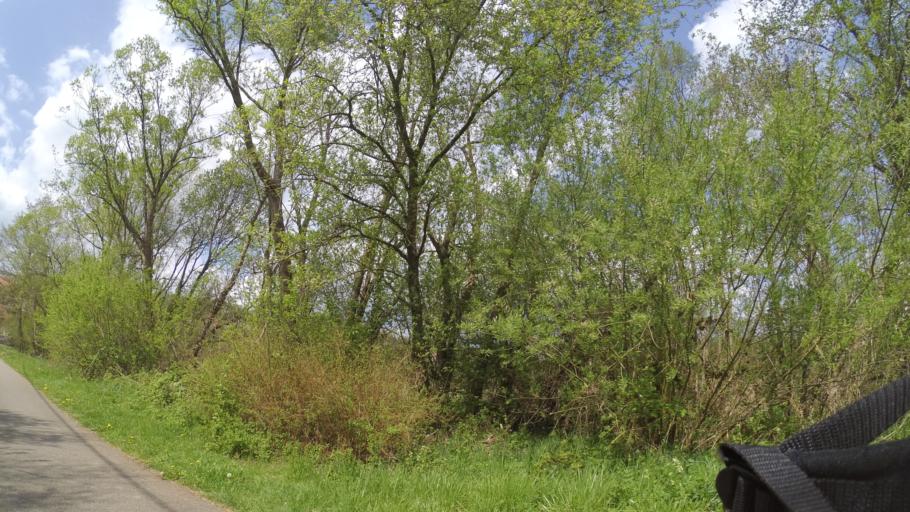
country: DE
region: Saarland
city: Wadern
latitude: 49.5710
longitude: 6.9266
